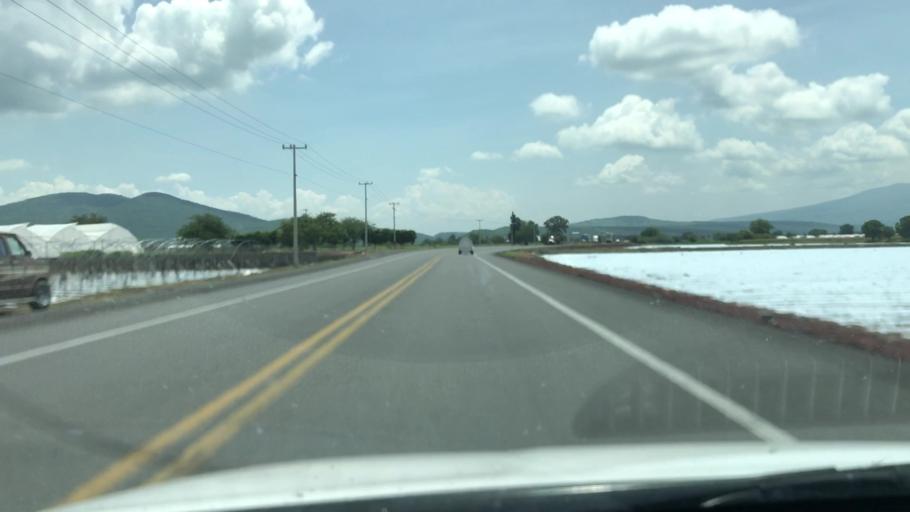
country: MX
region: Michoacan
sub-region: Yurecuaro
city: Yurecuaro
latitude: 20.3212
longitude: -102.2899
